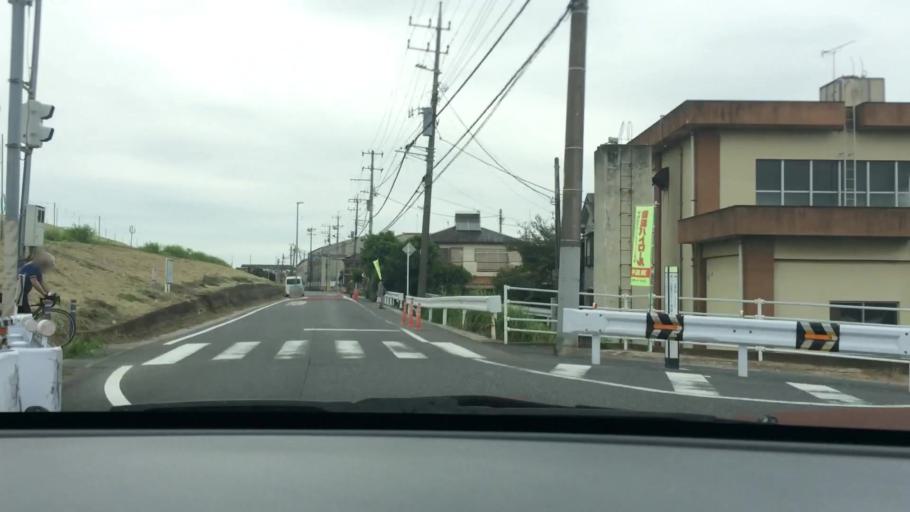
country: JP
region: Chiba
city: Nagareyama
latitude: 35.8521
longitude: 139.8968
